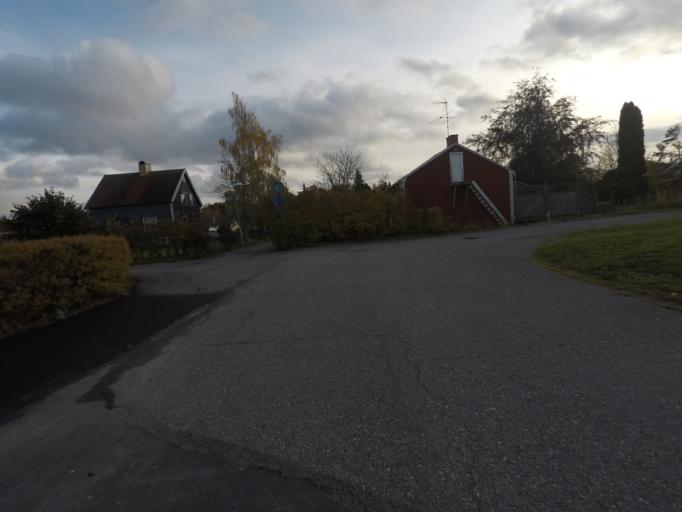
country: SE
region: OErebro
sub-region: Karlskoga Kommun
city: Karlskoga
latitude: 59.3089
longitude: 14.4814
